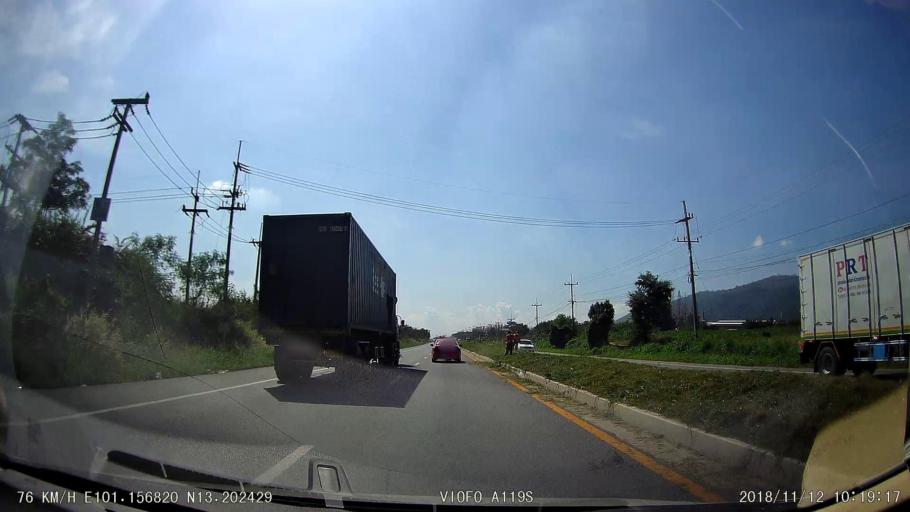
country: TH
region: Chon Buri
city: Ban Bueng
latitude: 13.2020
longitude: 101.1569
